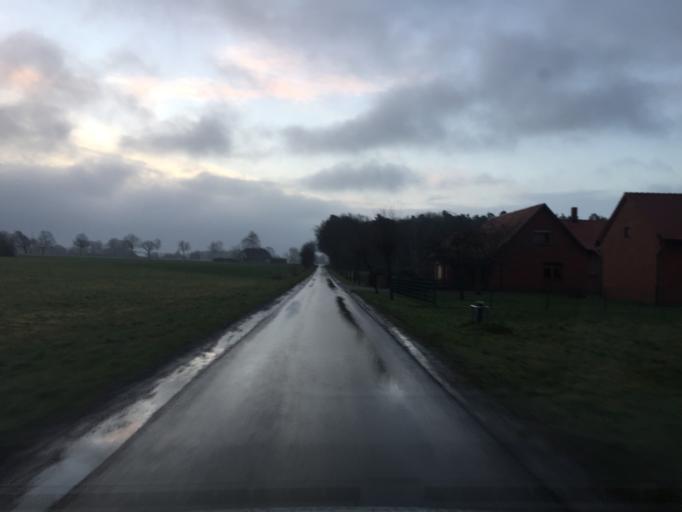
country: DE
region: Lower Saxony
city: Pennigsehl
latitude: 52.6555
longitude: 9.0282
